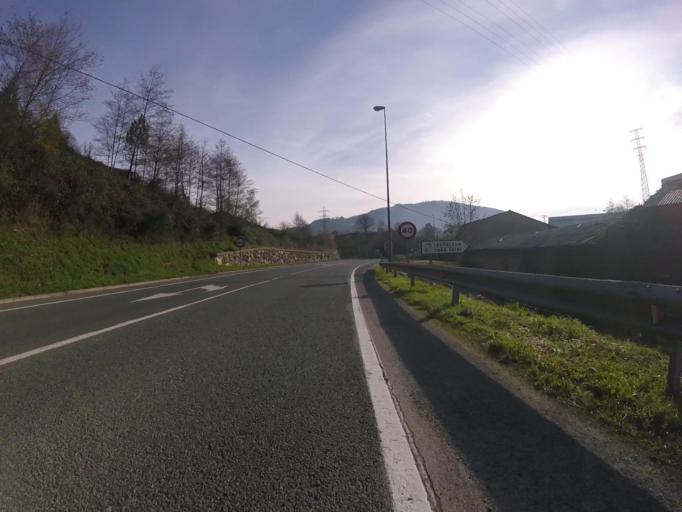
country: ES
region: Navarre
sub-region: Provincia de Navarra
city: Leitza
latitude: 43.0868
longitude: -1.9224
